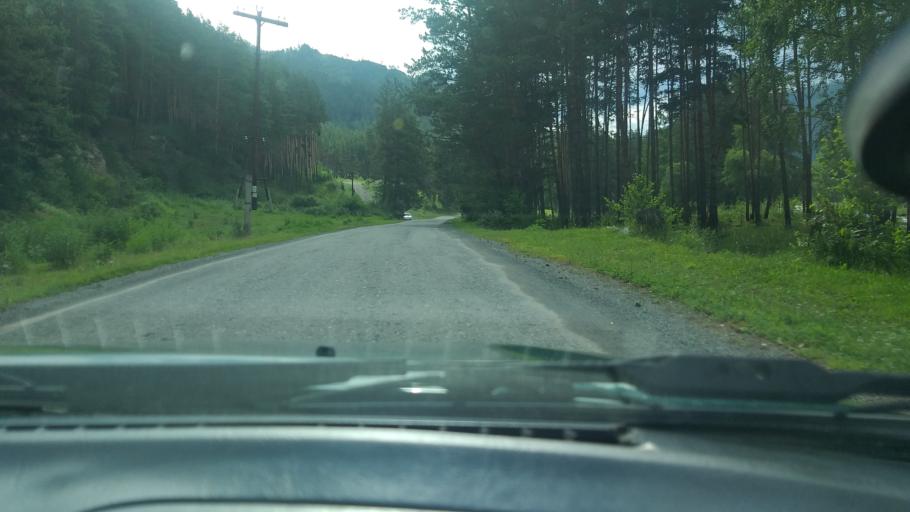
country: RU
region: Altay
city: Chemal
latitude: 51.3914
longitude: 86.0466
